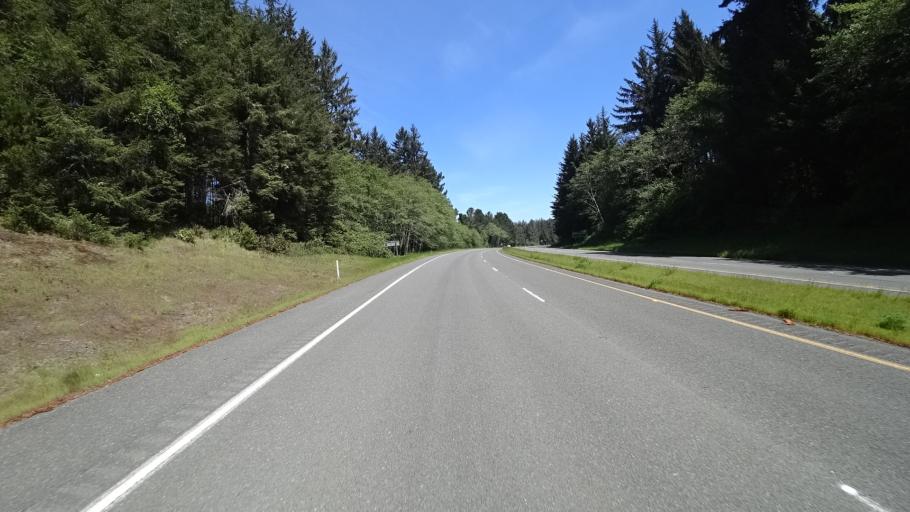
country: US
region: California
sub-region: Humboldt County
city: Westhaven-Moonstone
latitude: 41.1329
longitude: -124.1500
